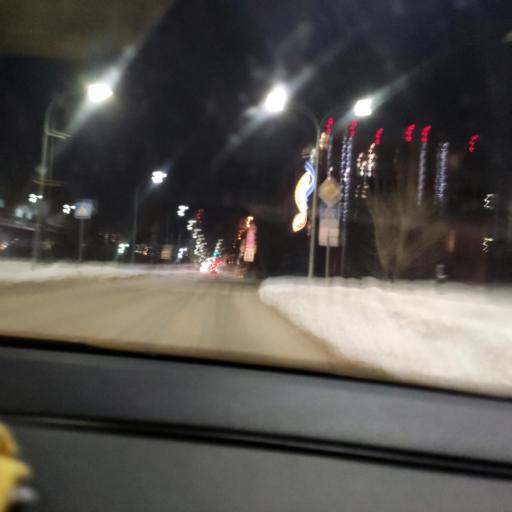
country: RU
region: Moskovskaya
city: Krasnogorsk
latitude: 55.8759
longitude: 37.3143
